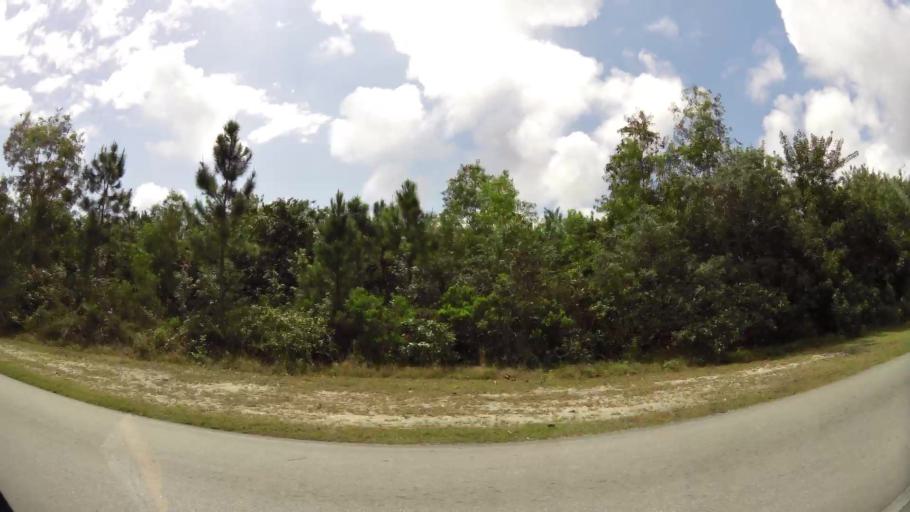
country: BS
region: Freeport
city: Lucaya
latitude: 26.5332
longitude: -78.6589
